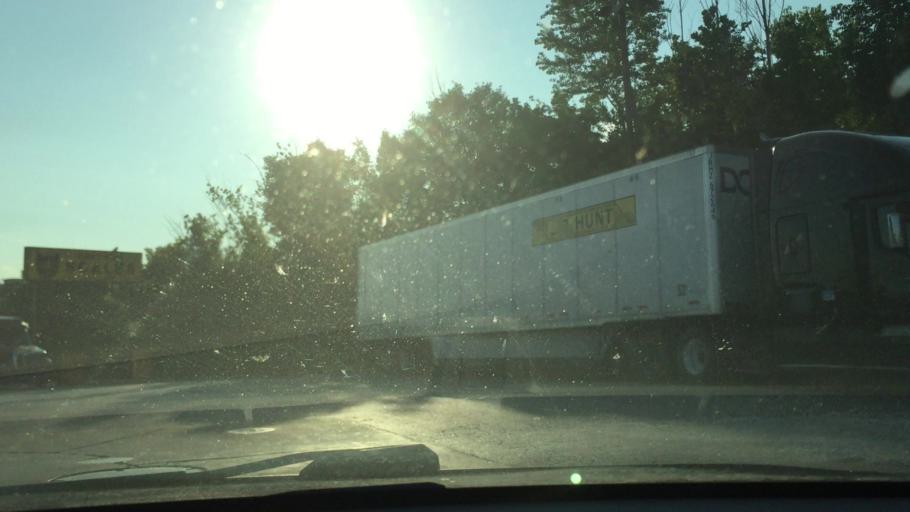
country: US
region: Kentucky
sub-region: Boone County
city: Walton
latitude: 38.9178
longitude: -84.6325
